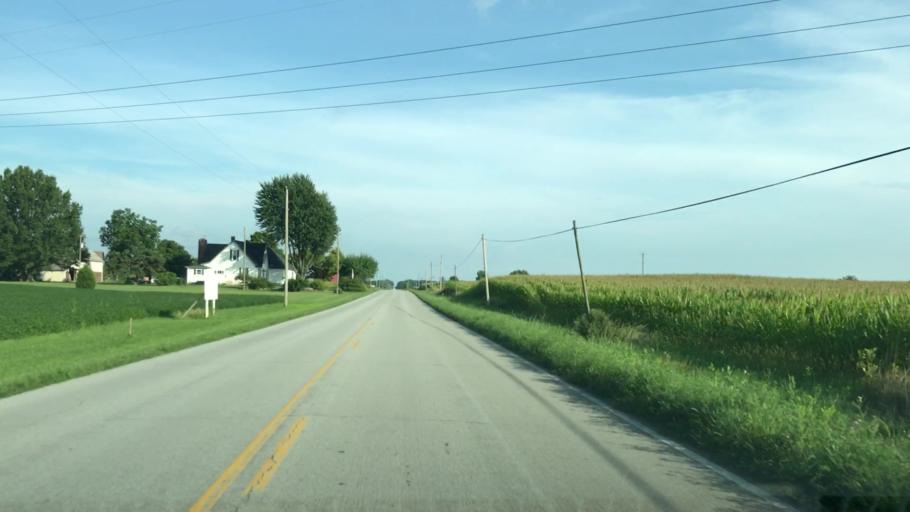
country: US
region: Ohio
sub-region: Union County
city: Marysville
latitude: 40.2061
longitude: -83.3514
